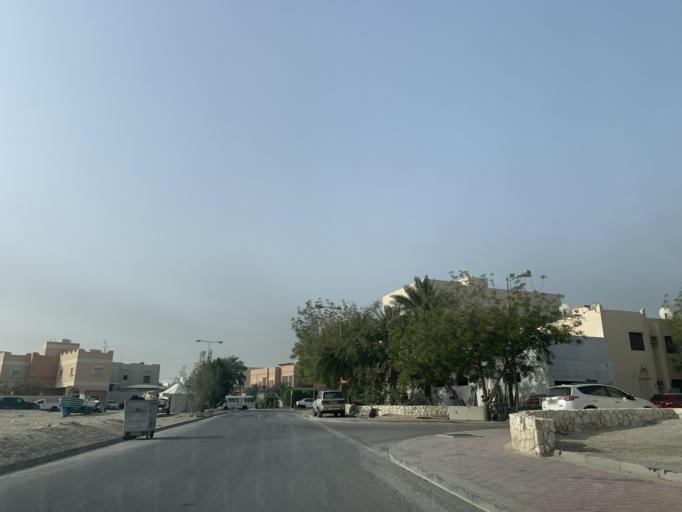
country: BH
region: Northern
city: Madinat `Isa
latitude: 26.1955
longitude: 50.5595
